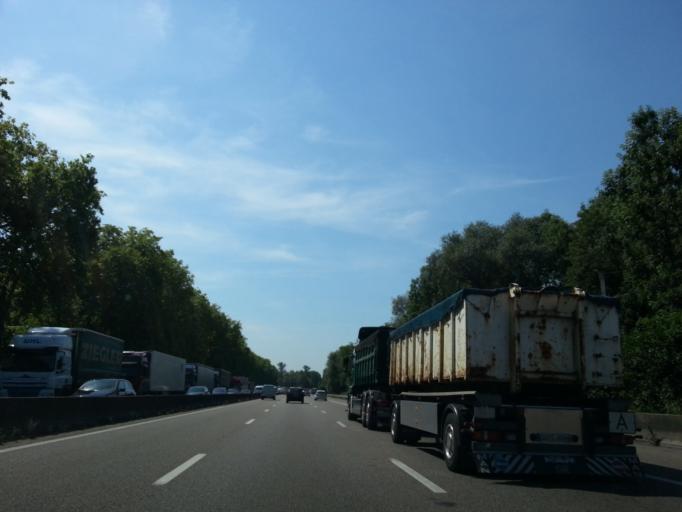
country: FR
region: Alsace
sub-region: Departement du Bas-Rhin
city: Ostwald
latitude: 48.5561
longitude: 7.7326
